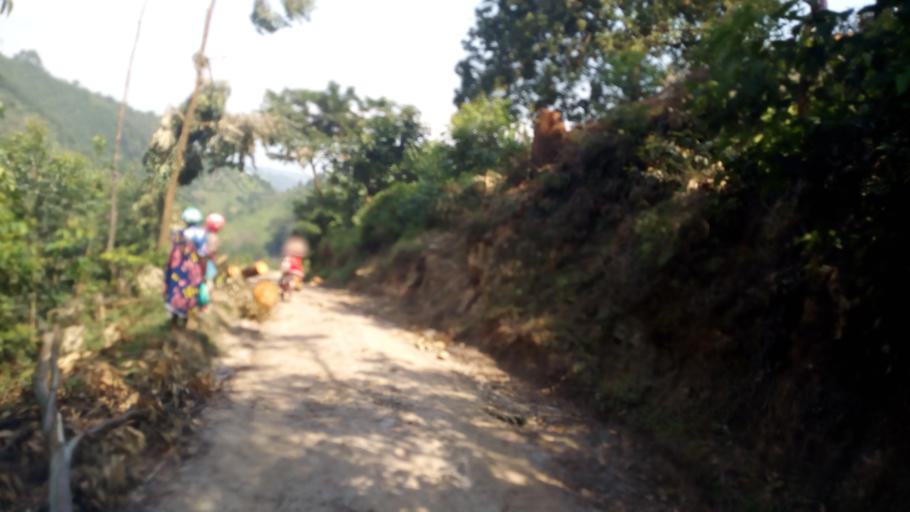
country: UG
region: Western Region
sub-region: Kisoro District
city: Kisoro
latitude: -1.1022
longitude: 29.5885
